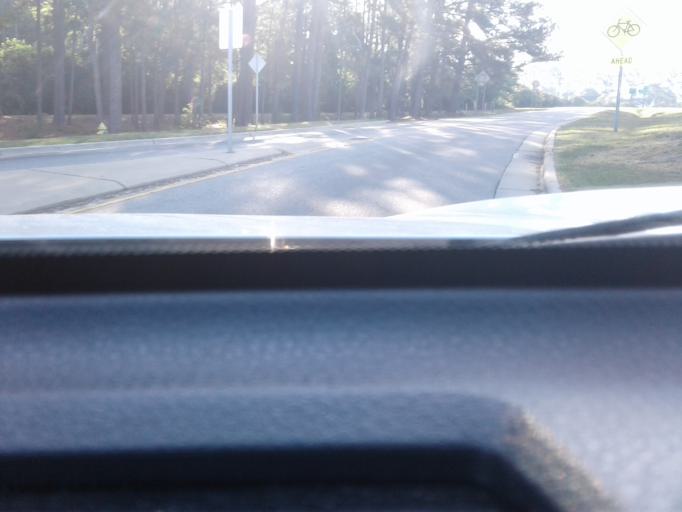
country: US
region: North Carolina
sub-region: Harnett County
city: Dunn
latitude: 35.3259
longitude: -78.6304
